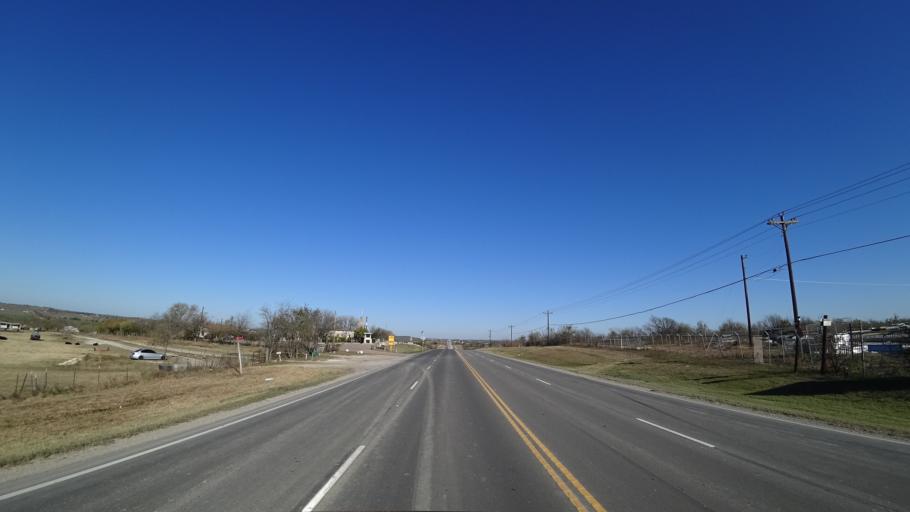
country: US
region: Texas
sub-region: Travis County
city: Onion Creek
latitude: 30.1186
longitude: -97.6953
